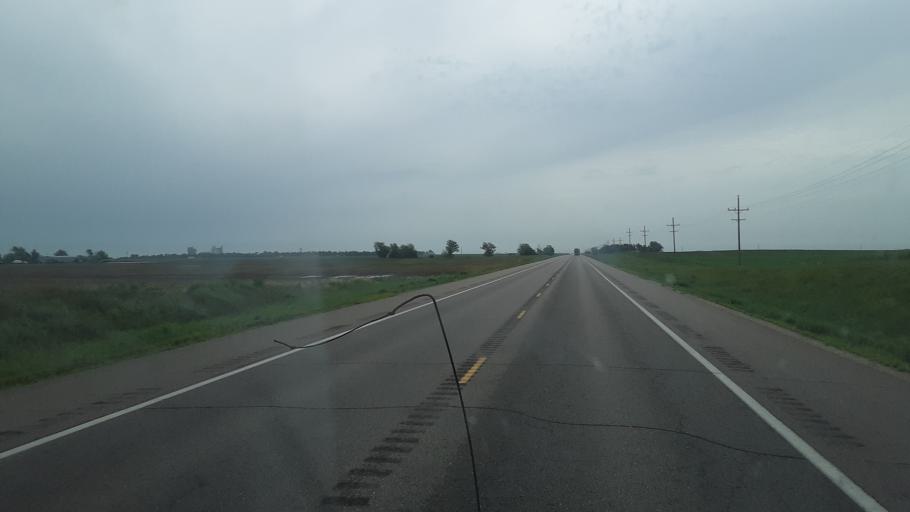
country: US
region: Kansas
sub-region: Edwards County
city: Kinsley
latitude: 37.9274
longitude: -99.2858
